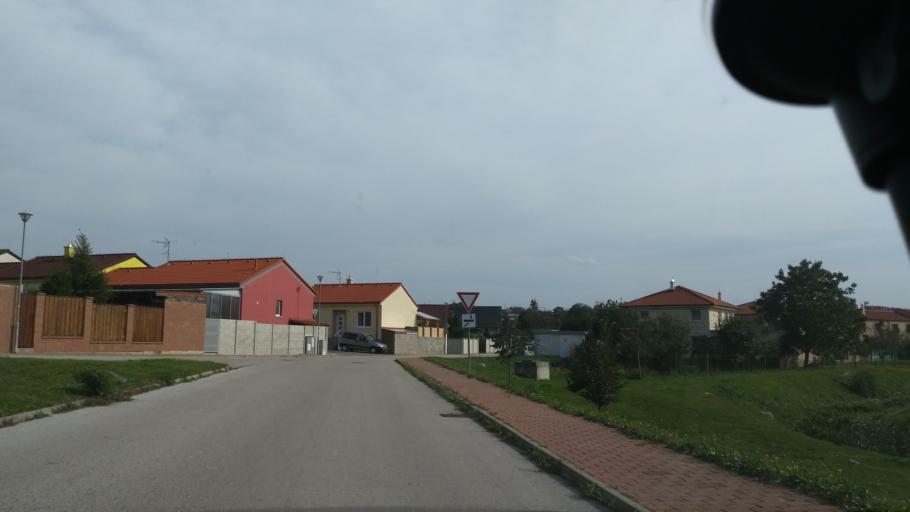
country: SK
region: Trnavsky
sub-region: Okres Skalica
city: Skalica
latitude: 48.8535
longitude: 17.2318
